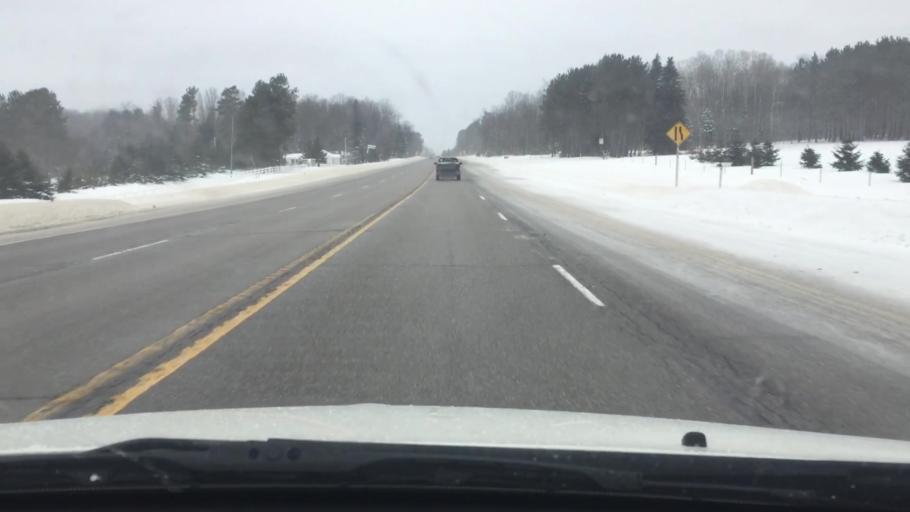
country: US
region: Michigan
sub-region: Otsego County
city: Gaylord
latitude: 45.0519
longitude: -84.7759
